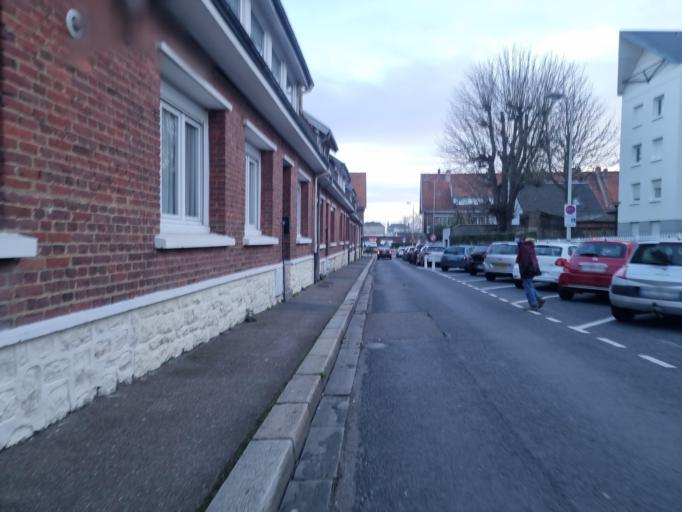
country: FR
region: Haute-Normandie
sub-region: Departement de la Seine-Maritime
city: Le Havre
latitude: 49.5065
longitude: 0.1019
